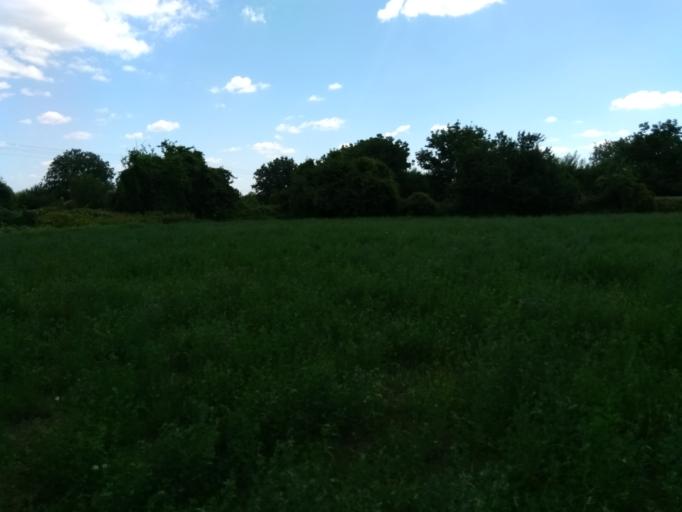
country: BG
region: Sliven
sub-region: Obshtina Nova Zagora
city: Nova Zagora
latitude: 42.5140
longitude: 25.9100
